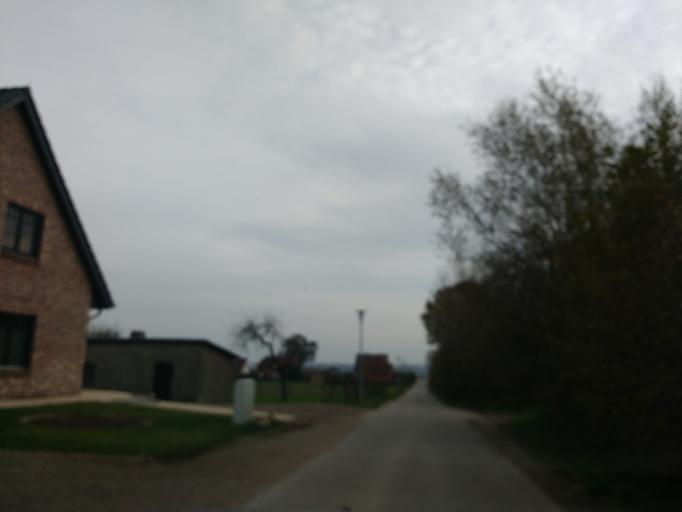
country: DE
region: Mecklenburg-Vorpommern
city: Klutz
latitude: 54.0015
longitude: 11.1660
